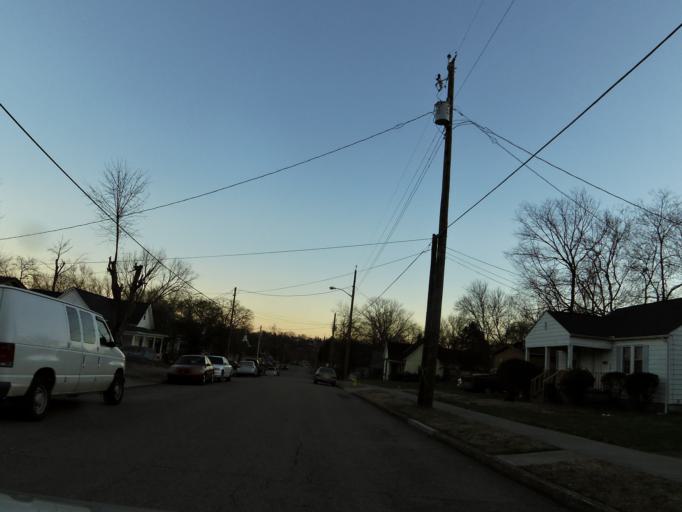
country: US
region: Tennessee
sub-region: Knox County
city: Knoxville
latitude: 35.9887
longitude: -83.9555
